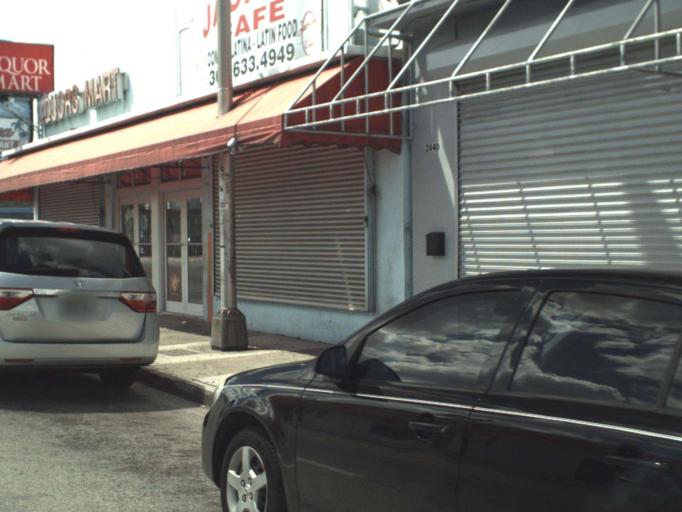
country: US
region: Florida
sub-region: Miami-Dade County
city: Allapattah
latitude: 25.8032
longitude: -80.2073
